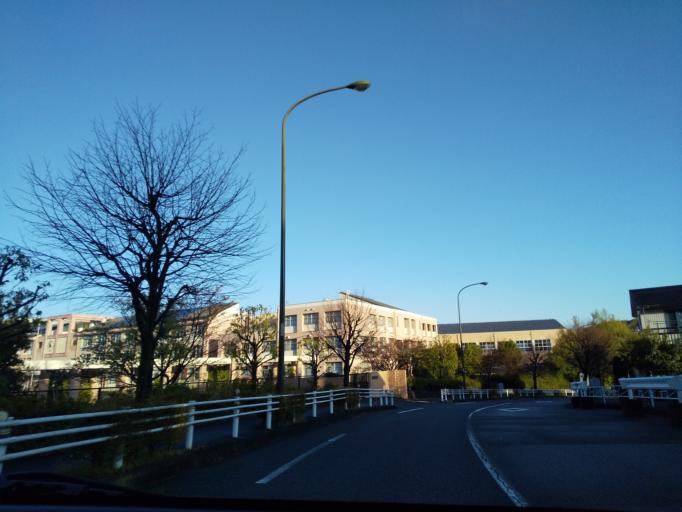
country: JP
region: Tokyo
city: Hachioji
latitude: 35.6124
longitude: 139.3611
